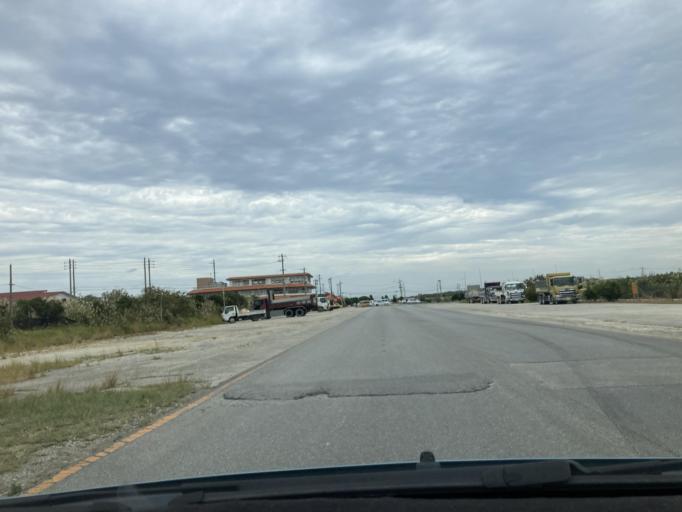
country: JP
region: Okinawa
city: Okinawa
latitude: 26.3914
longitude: 127.7465
